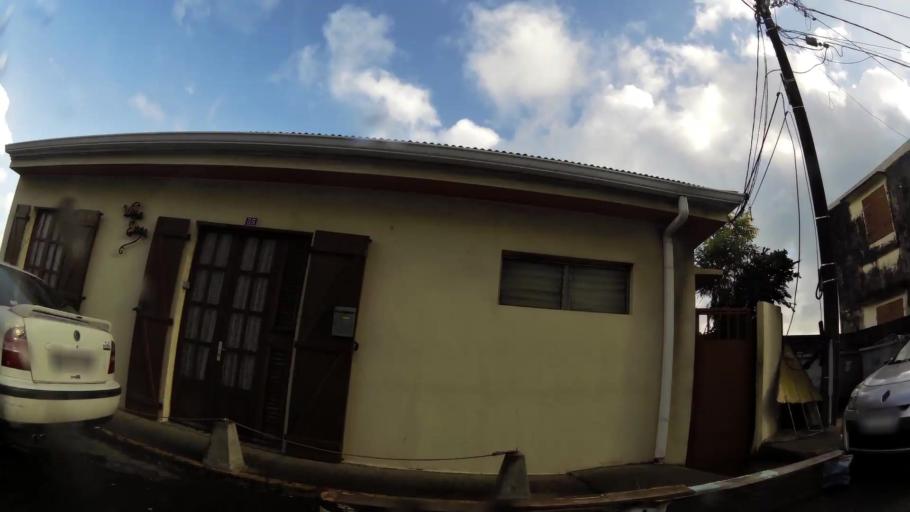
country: MQ
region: Martinique
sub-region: Martinique
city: Fort-de-France
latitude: 14.6050
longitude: -61.0751
